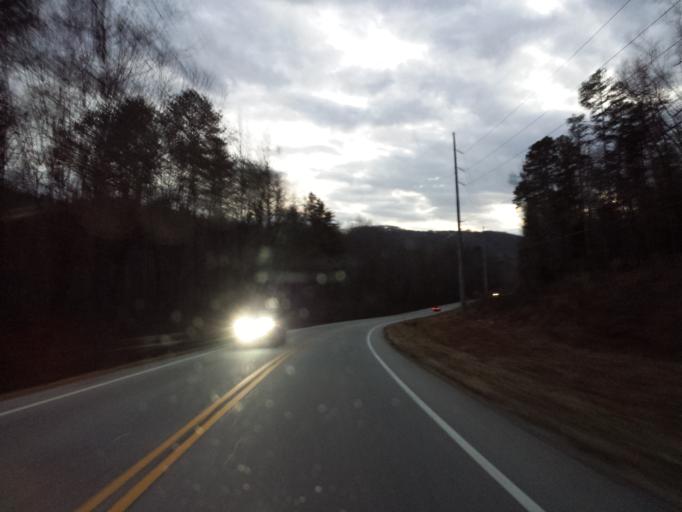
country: US
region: Georgia
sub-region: White County
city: Cleveland
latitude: 34.6694
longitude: -83.7142
